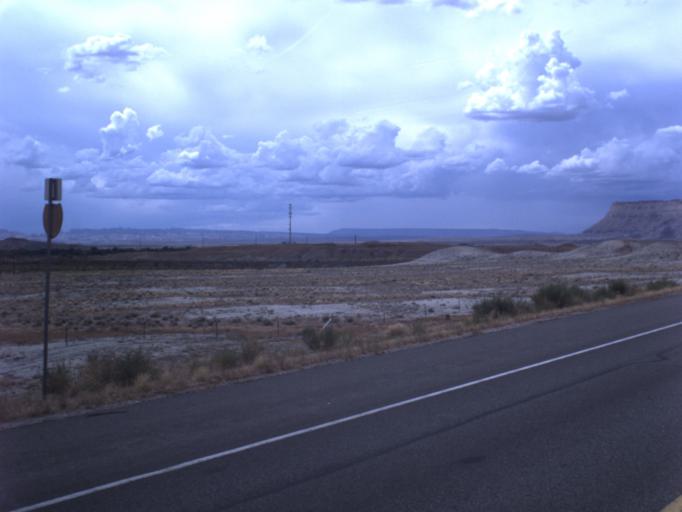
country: US
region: Utah
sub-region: Carbon County
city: East Carbon City
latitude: 38.9808
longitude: -110.1225
